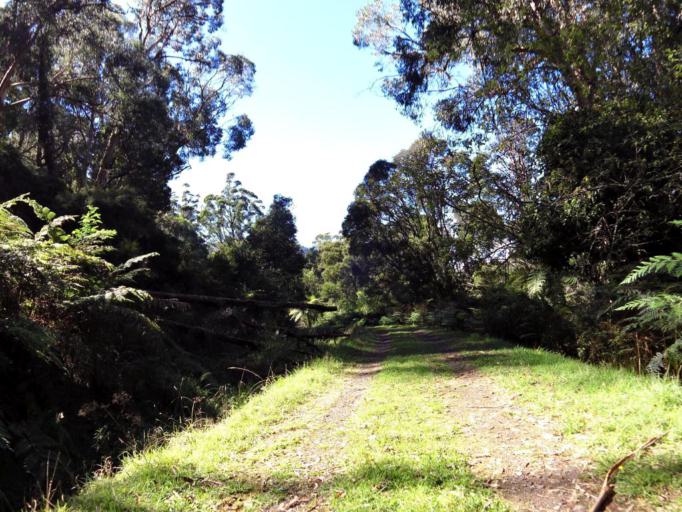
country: AU
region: Victoria
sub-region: Yarra Ranges
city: Launching Place
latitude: -37.7362
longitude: 145.5826
